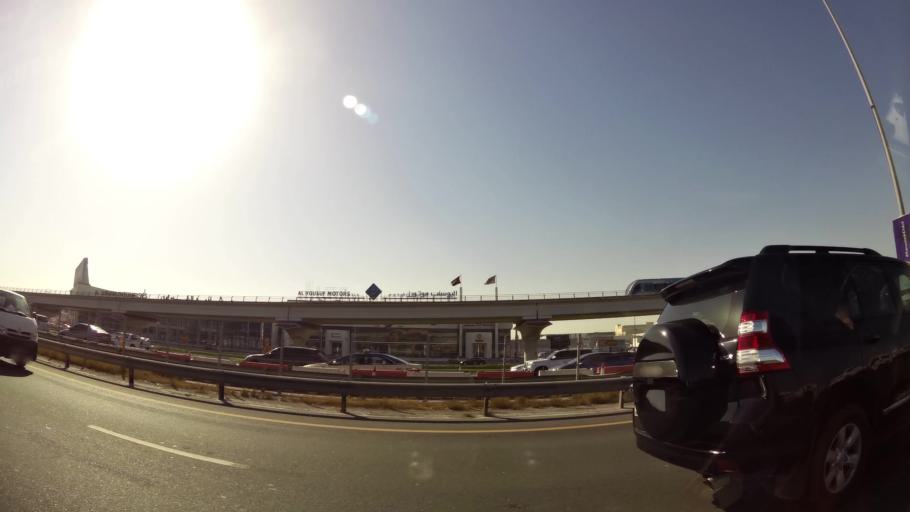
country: AE
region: Dubai
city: Dubai
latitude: 25.1574
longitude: 55.2288
